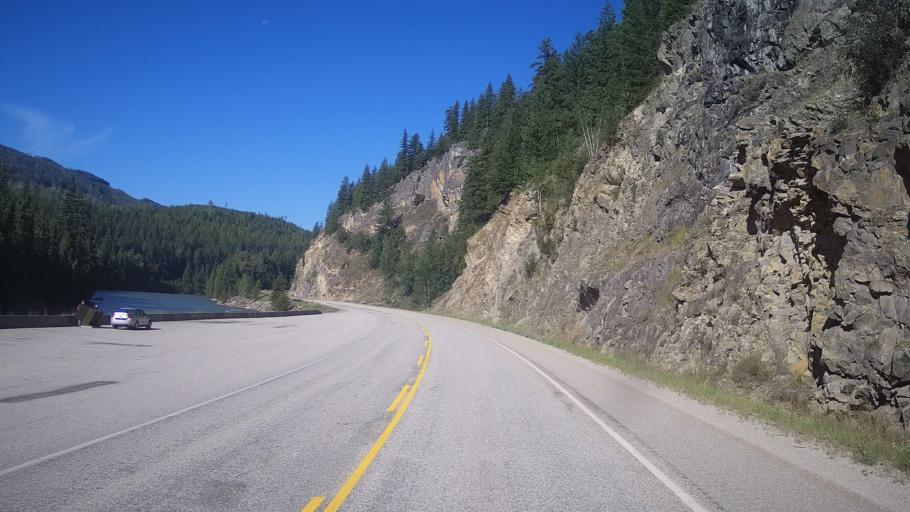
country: CA
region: British Columbia
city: Chase
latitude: 51.6716
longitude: -119.4739
